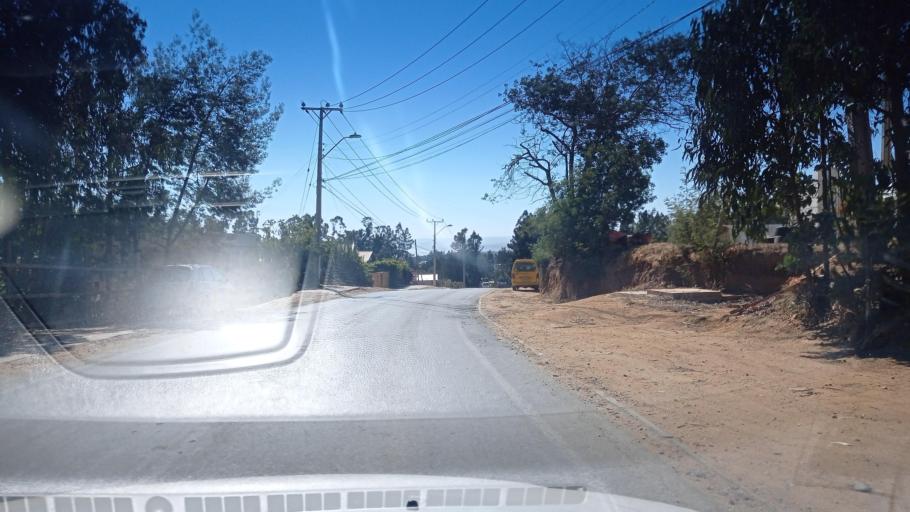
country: CL
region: O'Higgins
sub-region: Provincia de Colchagua
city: Santa Cruz
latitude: -34.4124
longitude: -71.9970
